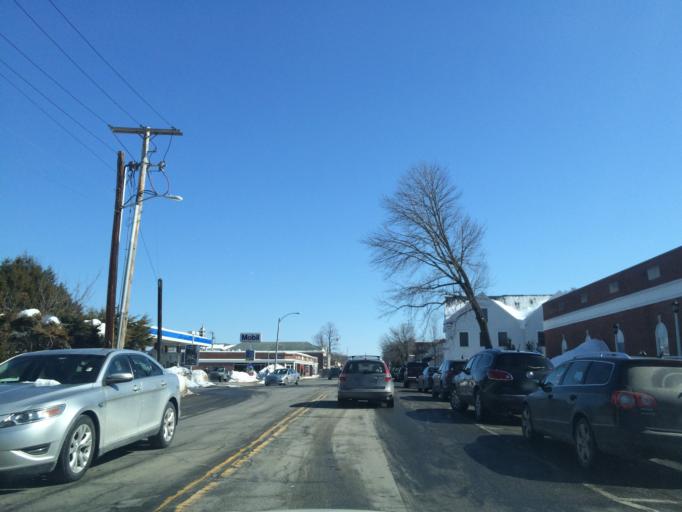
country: US
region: Massachusetts
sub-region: Norfolk County
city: Needham
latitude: 42.2802
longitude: -71.2403
